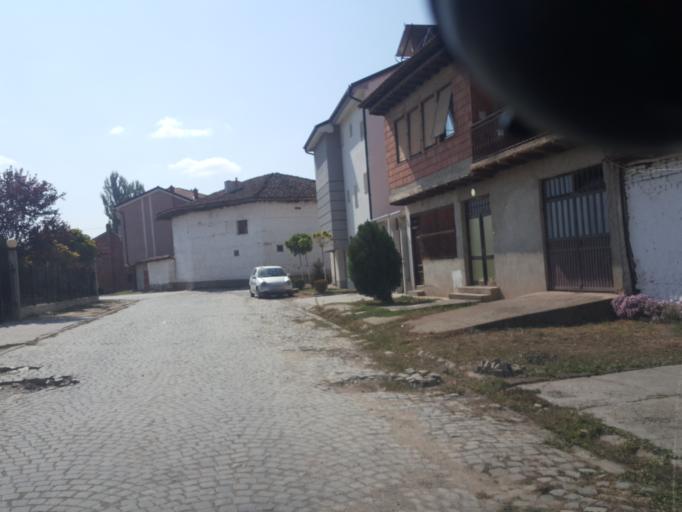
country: XK
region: Gjakova
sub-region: Komuna e Gjakoves
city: Gjakove
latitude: 42.3782
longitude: 20.4293
